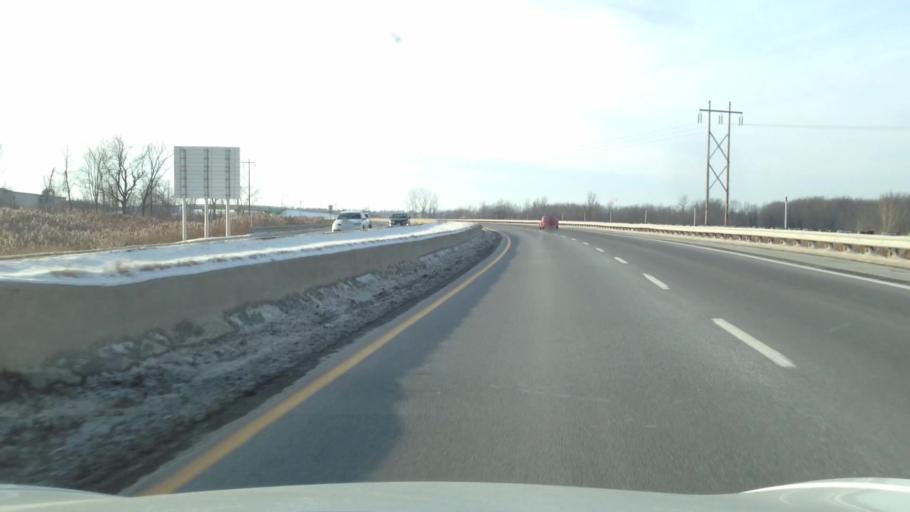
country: CA
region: Quebec
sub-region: Monteregie
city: Rigaud
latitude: 45.4881
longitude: -74.3059
